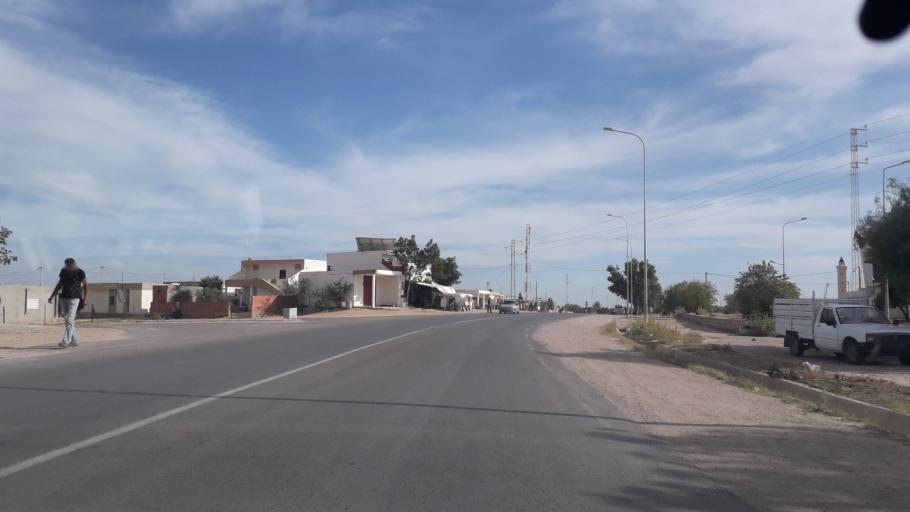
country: TN
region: Safaqis
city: Al Qarmadah
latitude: 34.8862
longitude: 10.7622
